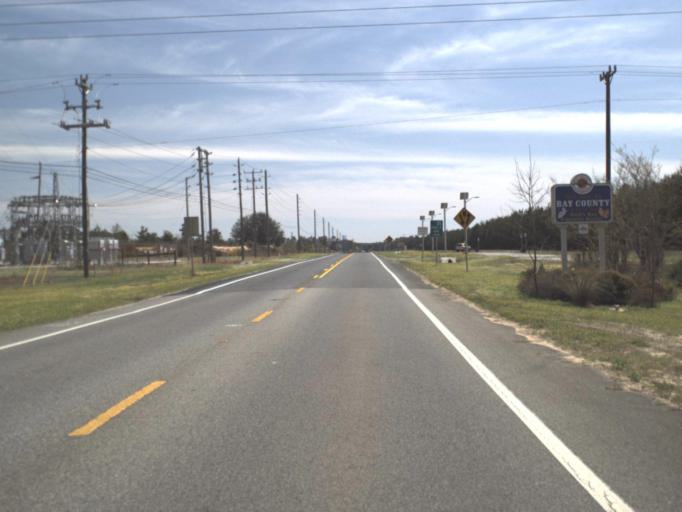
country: US
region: Florida
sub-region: Bay County
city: Lynn Haven
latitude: 30.4396
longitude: -85.6881
